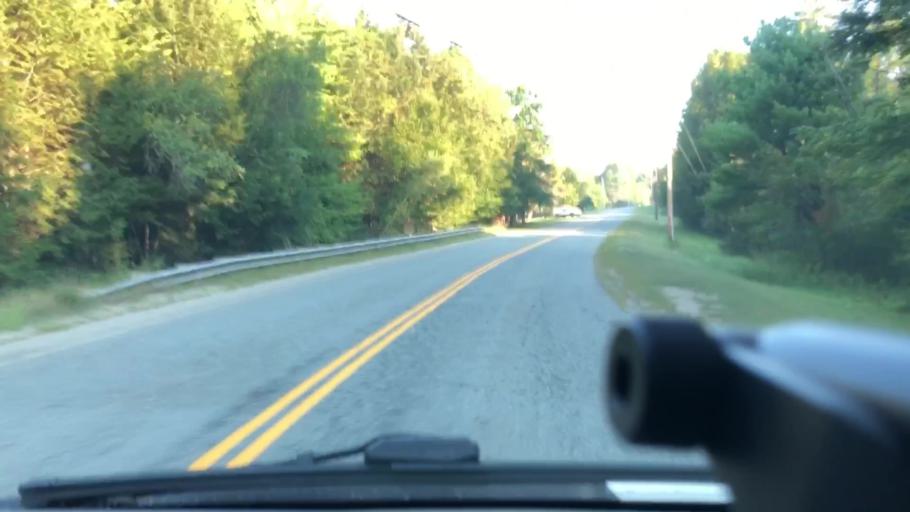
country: US
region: Massachusetts
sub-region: Franklin County
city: Ashfield
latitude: 42.5035
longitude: -72.8790
